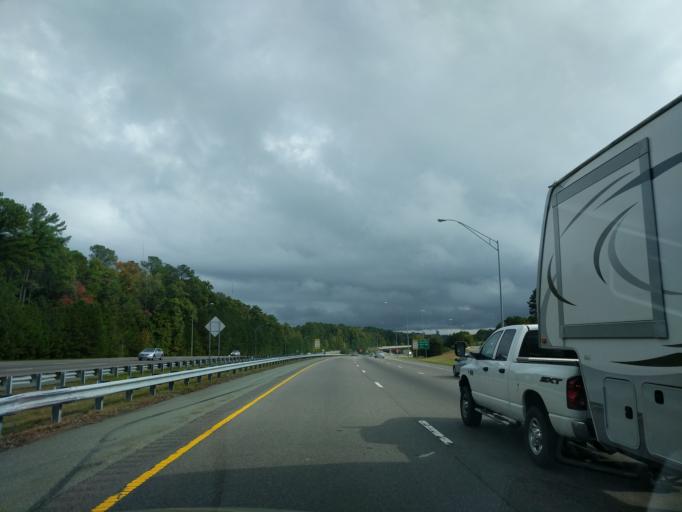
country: US
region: North Carolina
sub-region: Durham County
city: Durham
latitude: 36.0355
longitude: -78.9696
